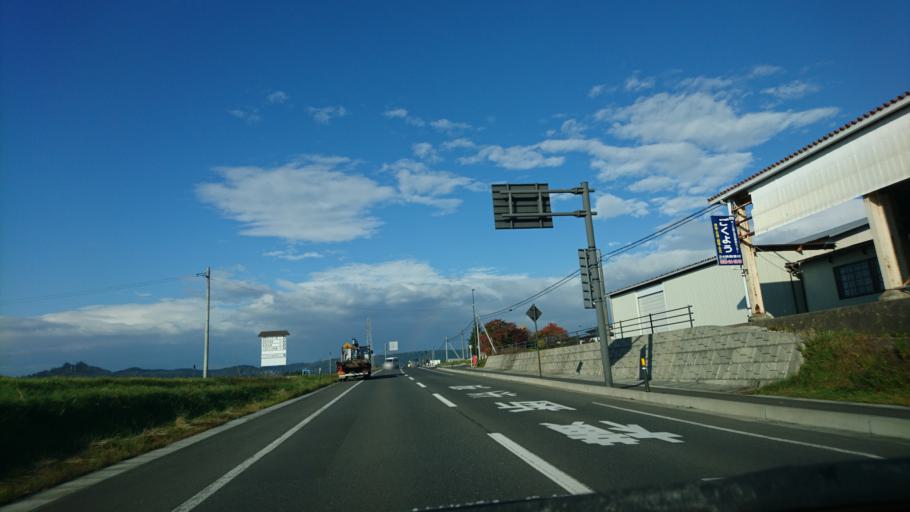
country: JP
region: Iwate
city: Ichinoseki
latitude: 39.0153
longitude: 141.1094
